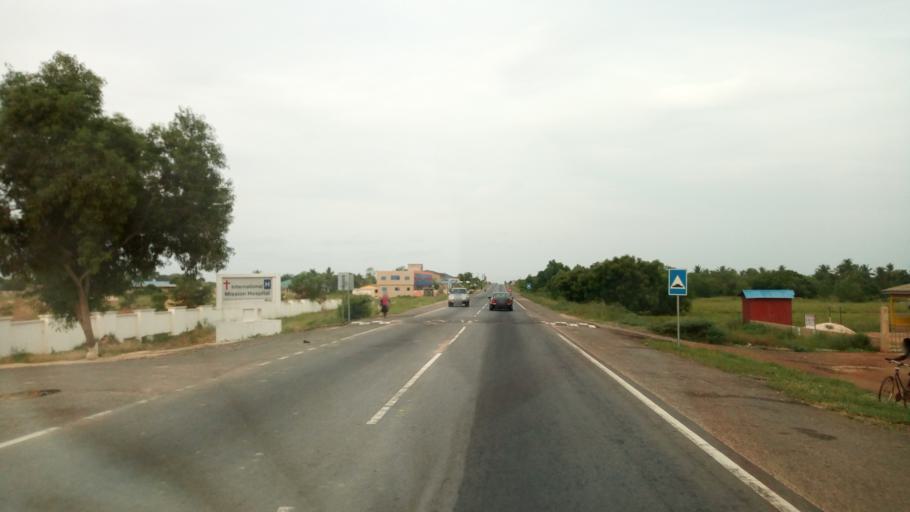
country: GH
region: Volta
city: Keta
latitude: 6.0585
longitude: 0.9920
